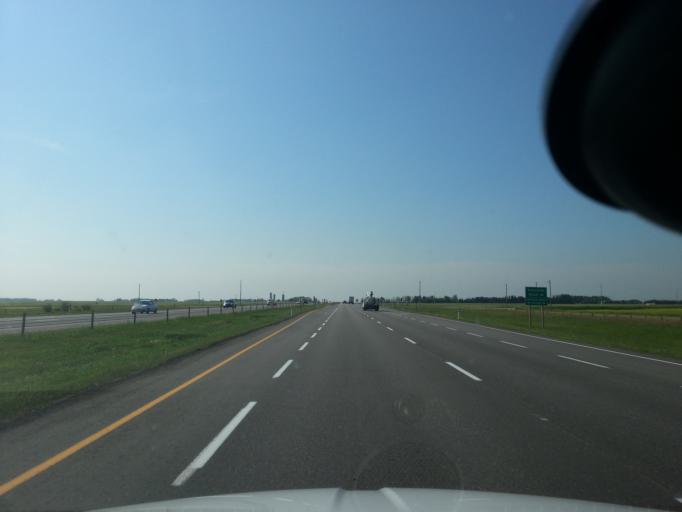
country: CA
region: Alberta
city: Olds
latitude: 51.7389
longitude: -114.0256
